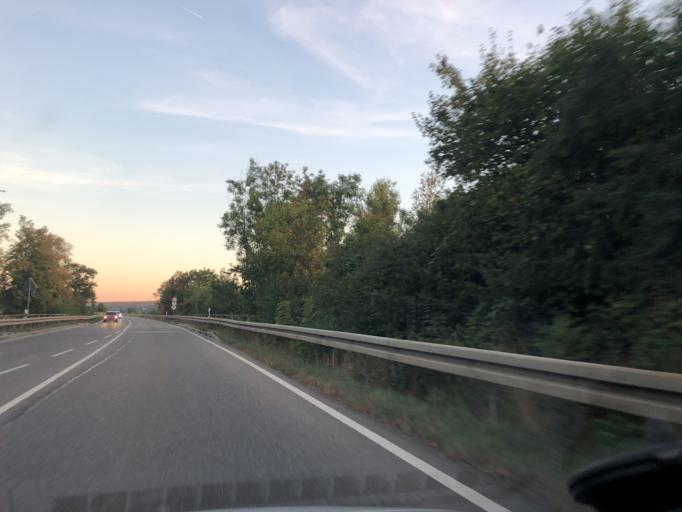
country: DE
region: Baden-Wuerttemberg
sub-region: Regierungsbezirk Stuttgart
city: Marbach am Neckar
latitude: 48.9004
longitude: 9.2617
